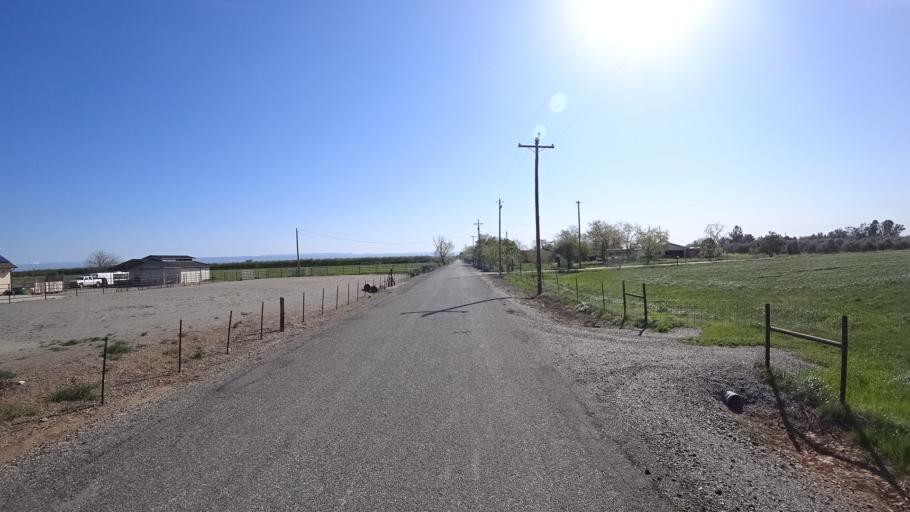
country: US
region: California
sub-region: Glenn County
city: Hamilton City
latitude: 39.7825
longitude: -122.0981
